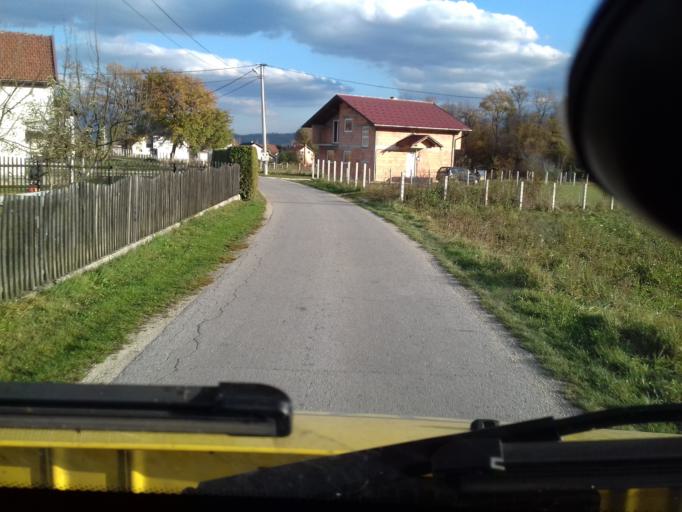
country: BA
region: Federation of Bosnia and Herzegovina
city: Vitez
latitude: 44.1555
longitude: 17.8038
